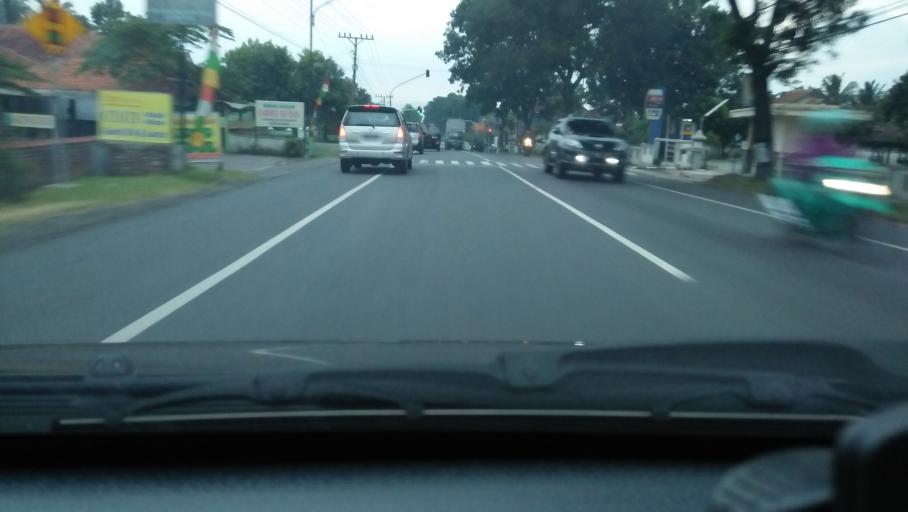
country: ID
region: Central Java
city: Magelang
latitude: -7.4051
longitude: 110.2394
